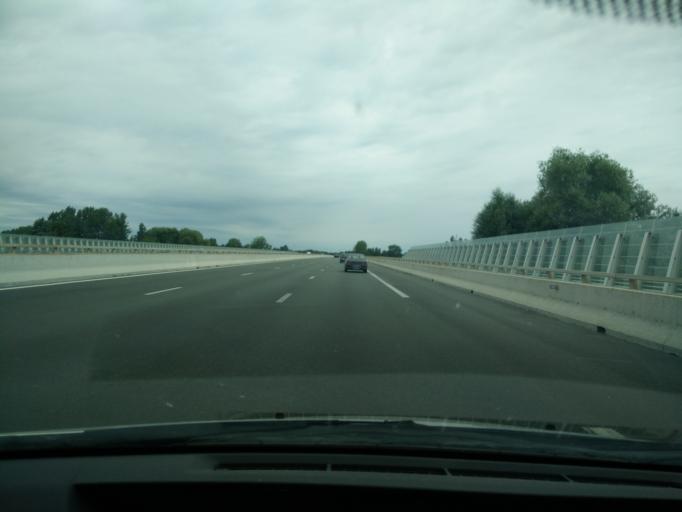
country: FR
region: Pays de la Loire
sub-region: Departement de Maine-et-Loire
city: Les Ponts-de-Ce
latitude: 47.4147
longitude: -0.5065
